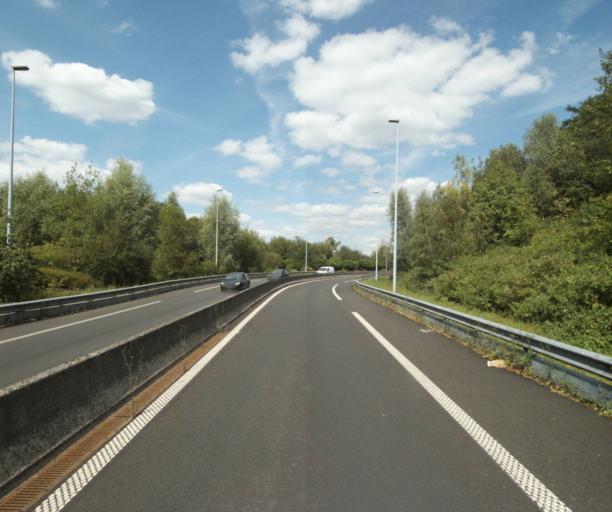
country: FR
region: Nord-Pas-de-Calais
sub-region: Departement du Nord
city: Mouvaux
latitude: 50.6902
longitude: 3.1399
